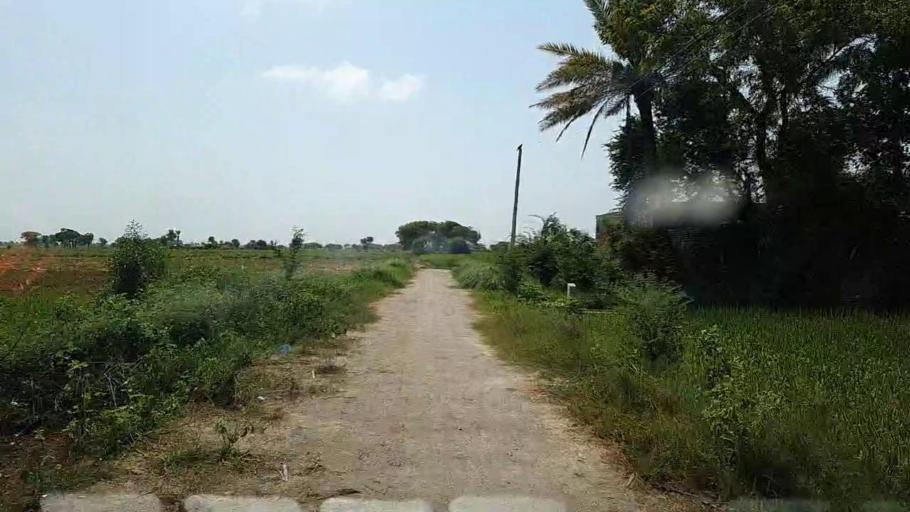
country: PK
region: Sindh
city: Kario
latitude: 24.6259
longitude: 68.5320
